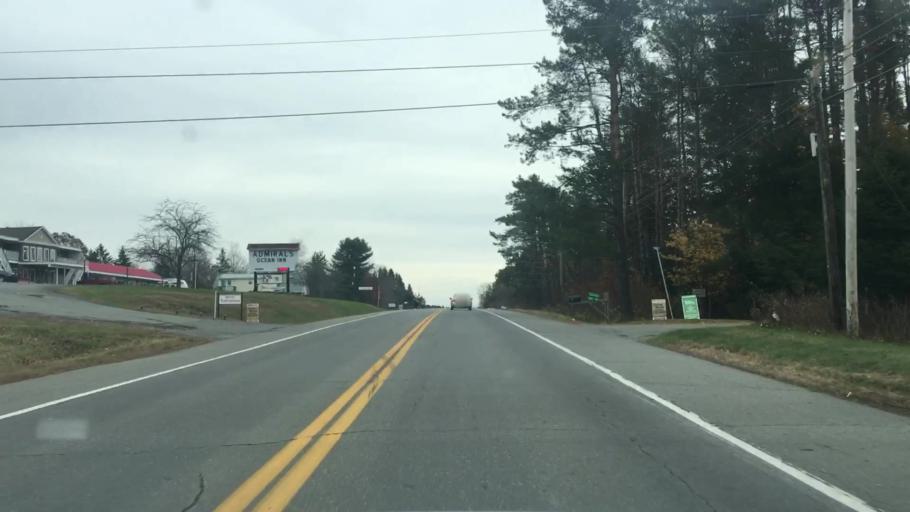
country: US
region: Maine
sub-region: Waldo County
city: Belfast
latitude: 44.4306
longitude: -68.9666
